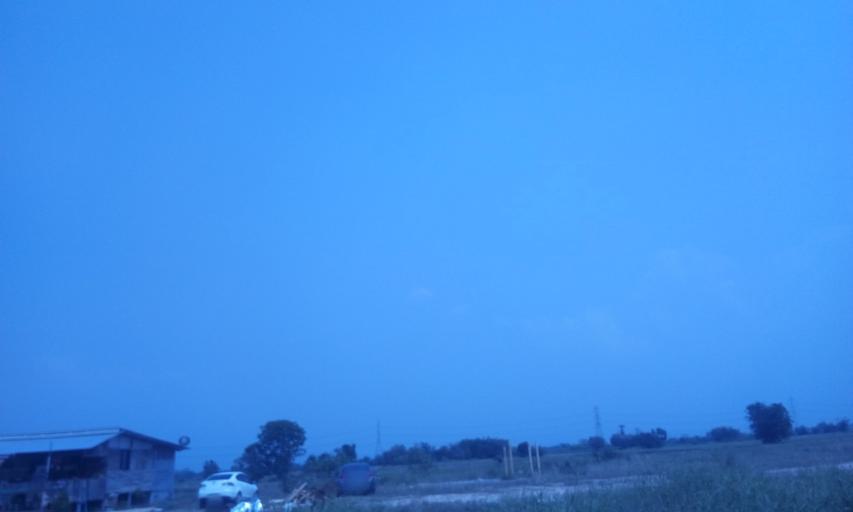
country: TH
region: Chon Buri
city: Phanat Nikhom
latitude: 13.4055
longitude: 101.1902
